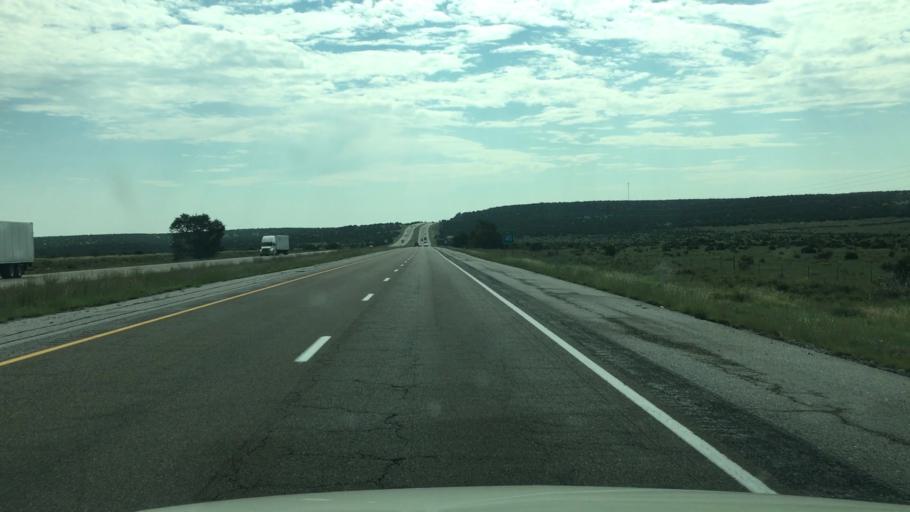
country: US
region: New Mexico
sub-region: Torrance County
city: Moriarty
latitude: 35.0055
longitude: -105.5150
